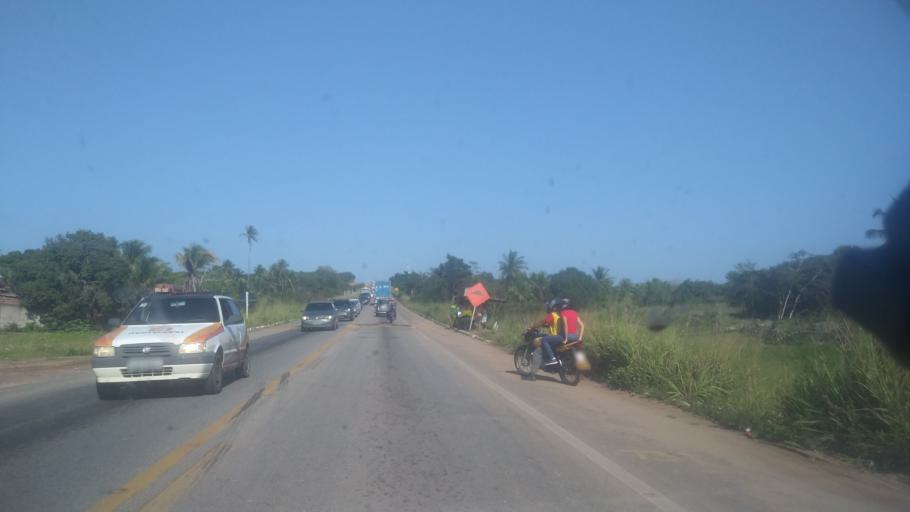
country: BR
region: Rio Grande do Norte
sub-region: Macaiba
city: Macaiba
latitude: -5.8664
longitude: -35.3608
